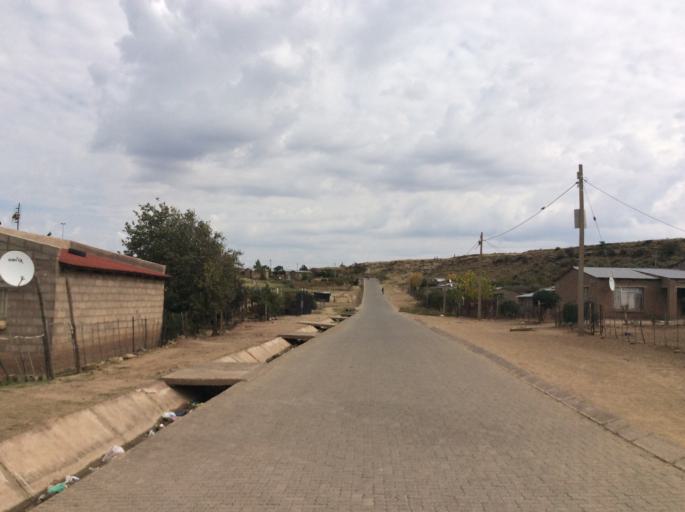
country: LS
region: Mafeteng
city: Mafeteng
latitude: -29.7176
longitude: 27.0202
